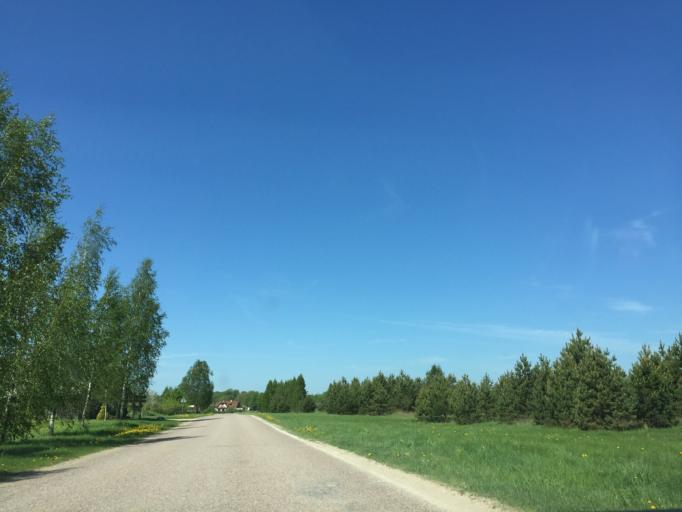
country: LV
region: Ogre
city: Ogre
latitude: 56.8531
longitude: 24.7082
